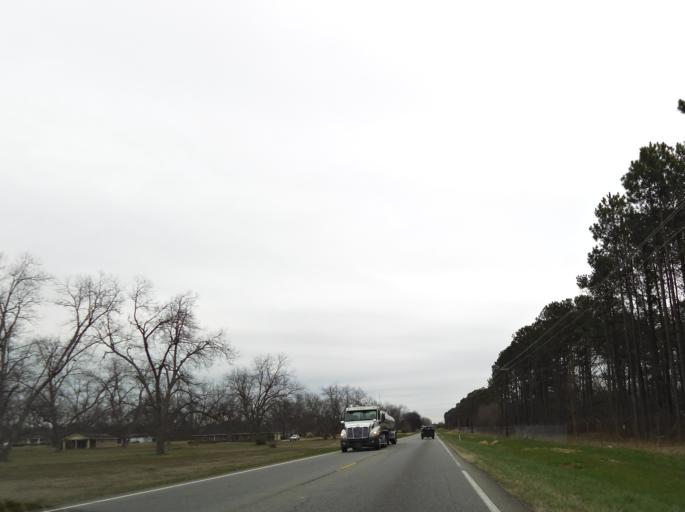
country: US
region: Georgia
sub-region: Peach County
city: Byron
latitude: 32.6665
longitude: -83.7343
